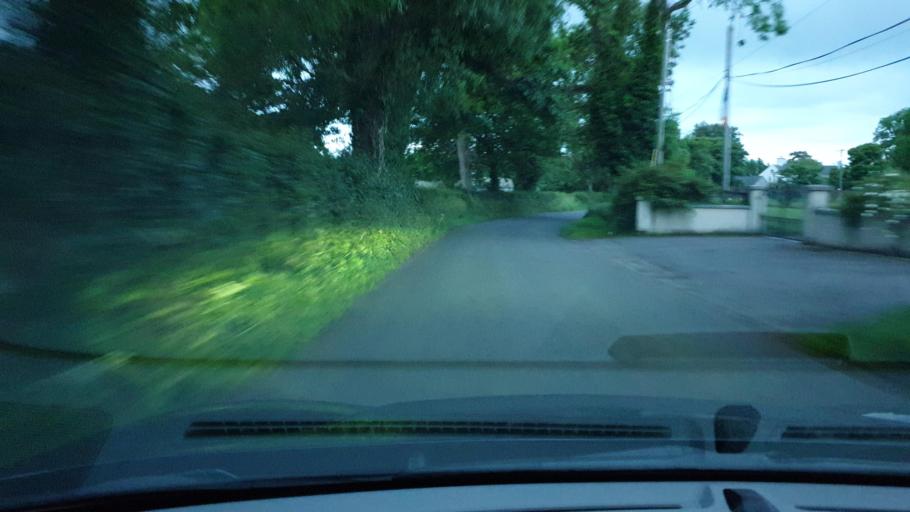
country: IE
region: Leinster
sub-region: An Mhi
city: Ashbourne
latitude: 53.5005
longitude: -6.3662
